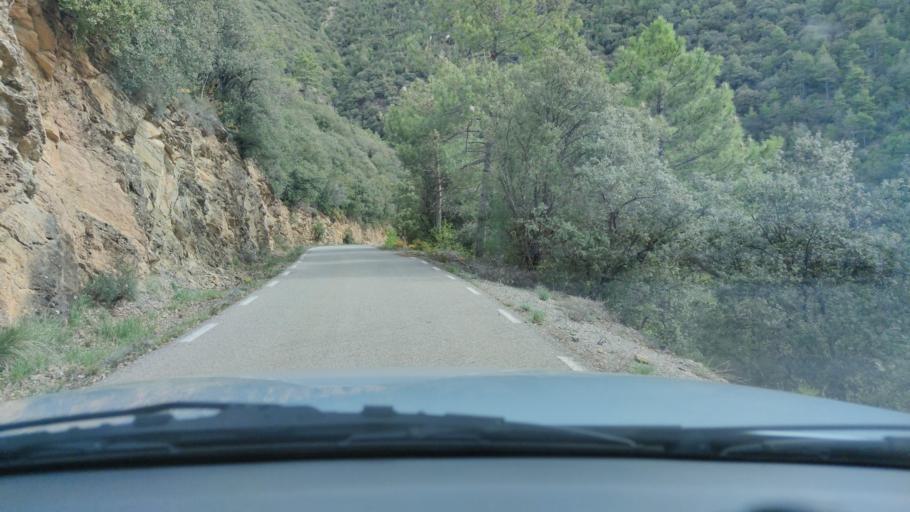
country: ES
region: Catalonia
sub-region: Provincia de Lleida
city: la Seu d'Urgell
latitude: 42.2427
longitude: 1.4294
